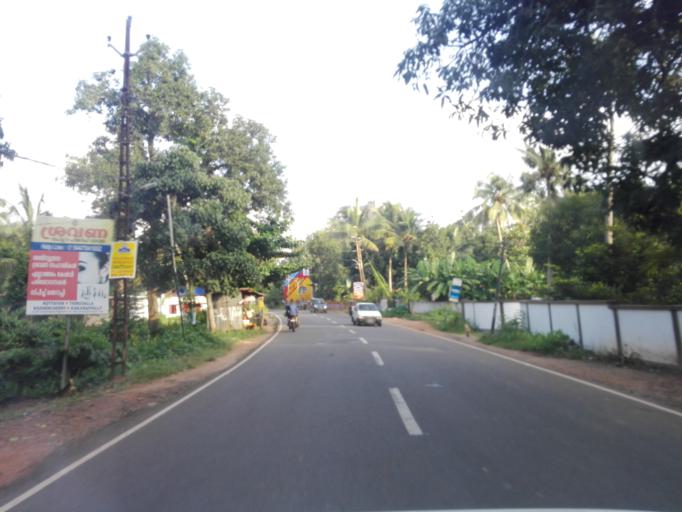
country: IN
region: Kerala
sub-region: Kottayam
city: Kottayam
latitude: 9.6102
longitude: 76.5082
